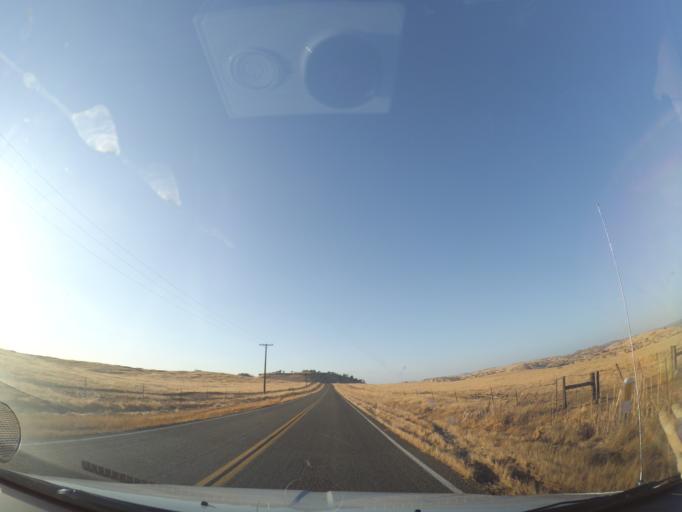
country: US
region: California
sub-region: Merced County
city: Planada
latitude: 37.5010
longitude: -120.3137
